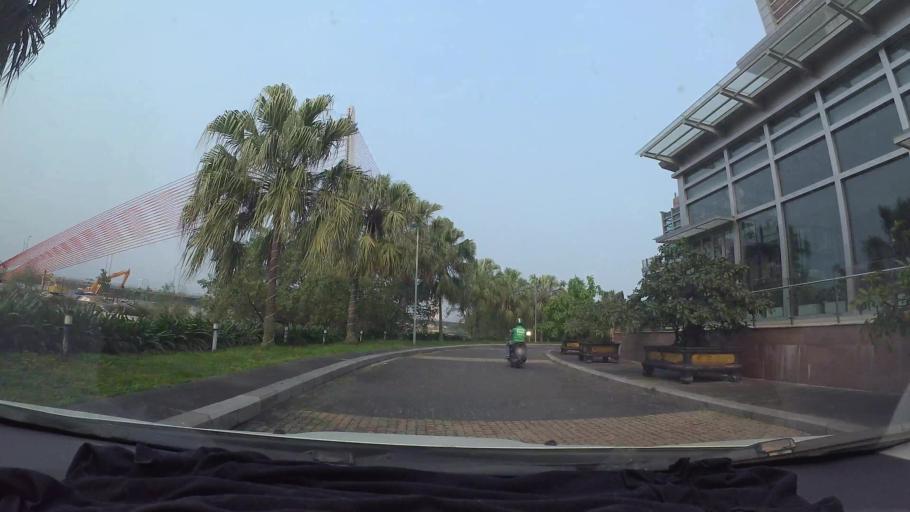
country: VN
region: Da Nang
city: Son Tra
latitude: 16.0485
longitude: 108.2266
